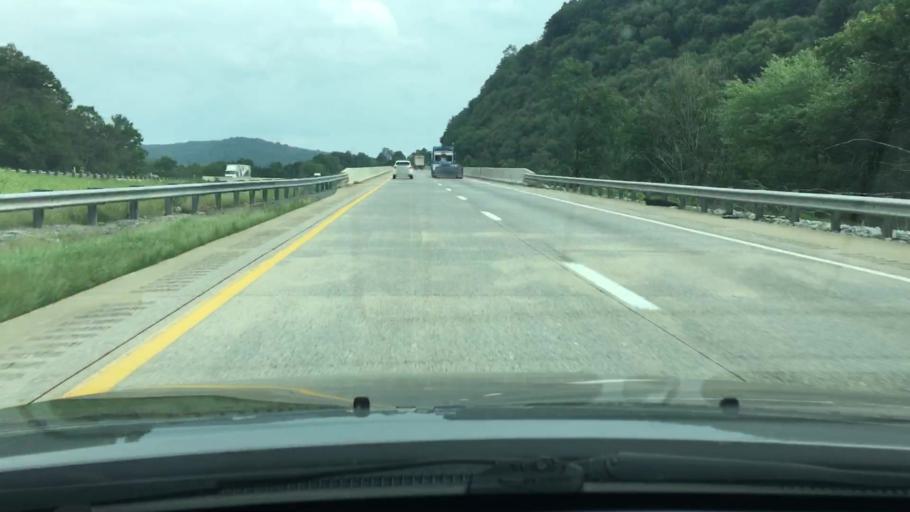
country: US
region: Pennsylvania
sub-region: Lebanon County
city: Jonestown
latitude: 40.4794
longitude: -76.5290
